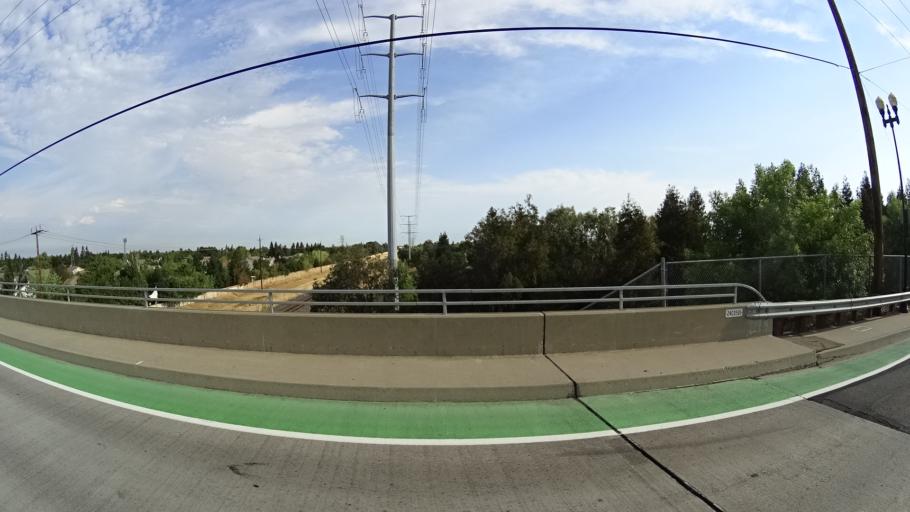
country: US
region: California
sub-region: Sacramento County
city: Laguna
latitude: 38.4087
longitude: -121.4543
